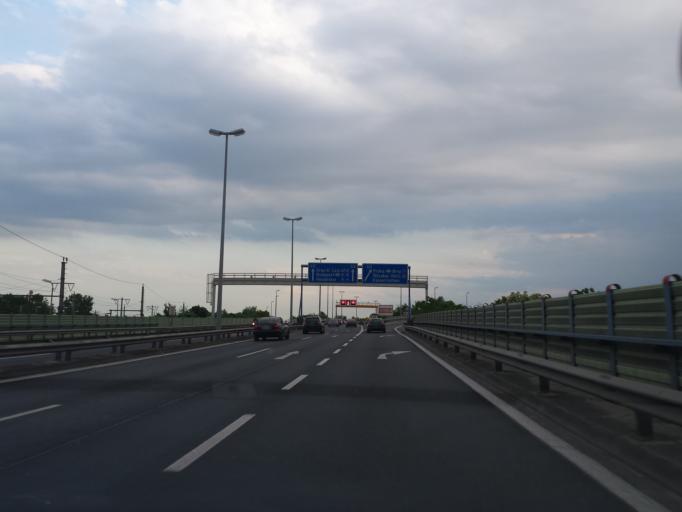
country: AT
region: Vienna
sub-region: Wien Stadt
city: Vienna
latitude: 48.2175
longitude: 16.4469
